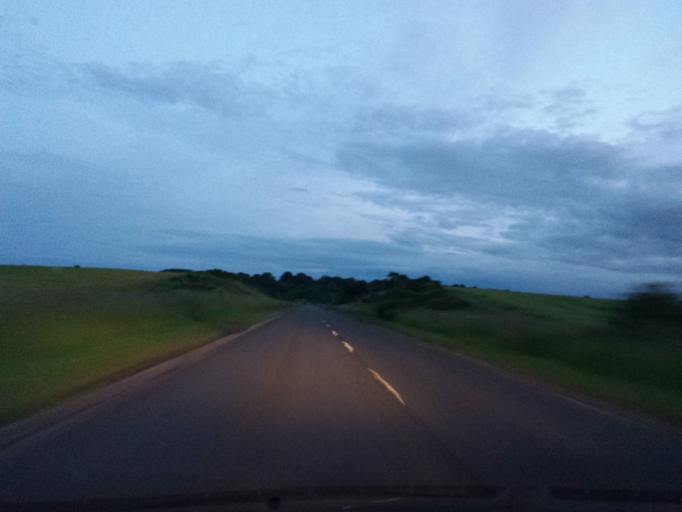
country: GB
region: Scotland
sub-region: The Scottish Borders
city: Duns
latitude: 55.7511
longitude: -2.4063
